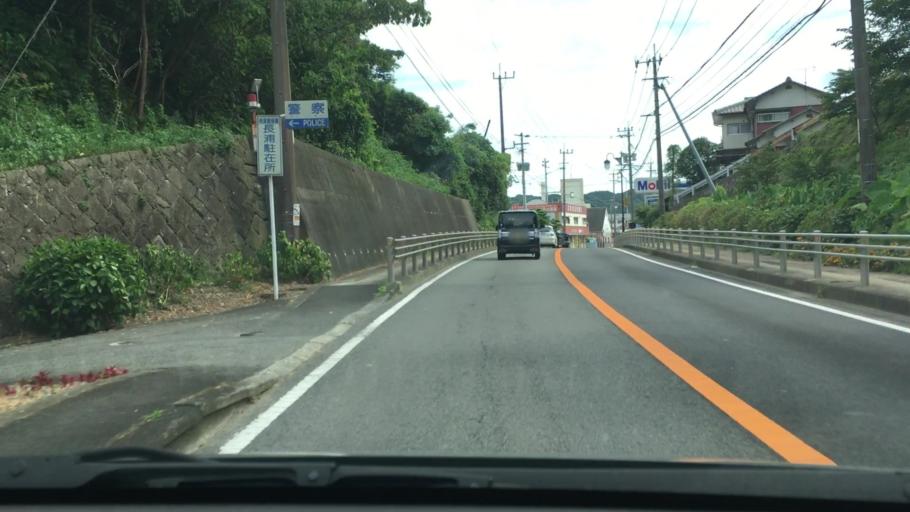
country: JP
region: Nagasaki
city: Togitsu
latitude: 32.9111
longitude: 129.7844
